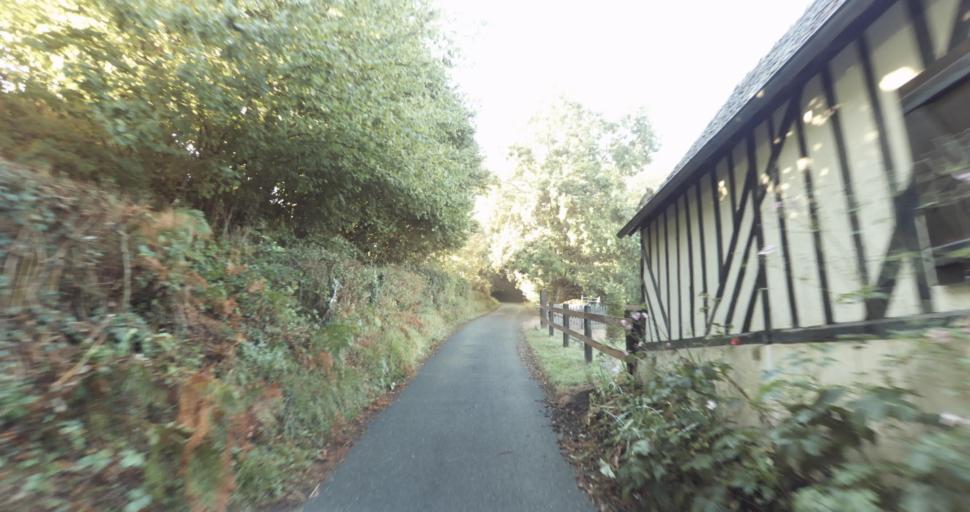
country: FR
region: Lower Normandy
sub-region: Departement de l'Orne
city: Vimoutiers
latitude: 48.9205
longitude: 0.1739
